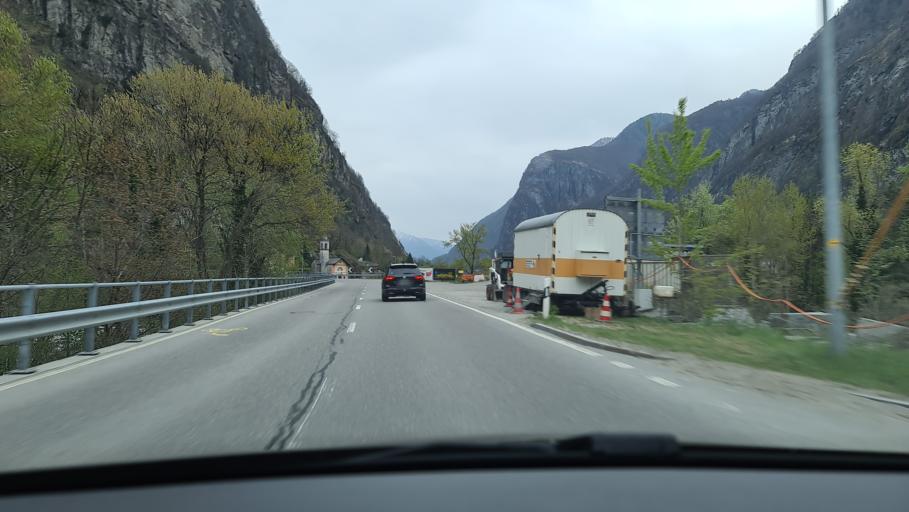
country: CH
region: Ticino
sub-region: Vallemaggia District
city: Cevio
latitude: 46.3097
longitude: 8.6080
